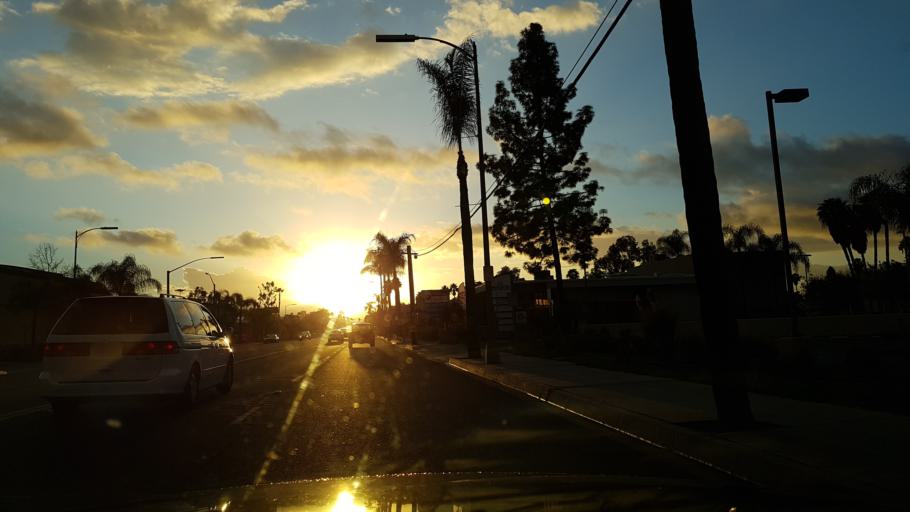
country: US
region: California
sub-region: San Diego County
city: Escondido
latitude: 33.1335
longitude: -117.0607
